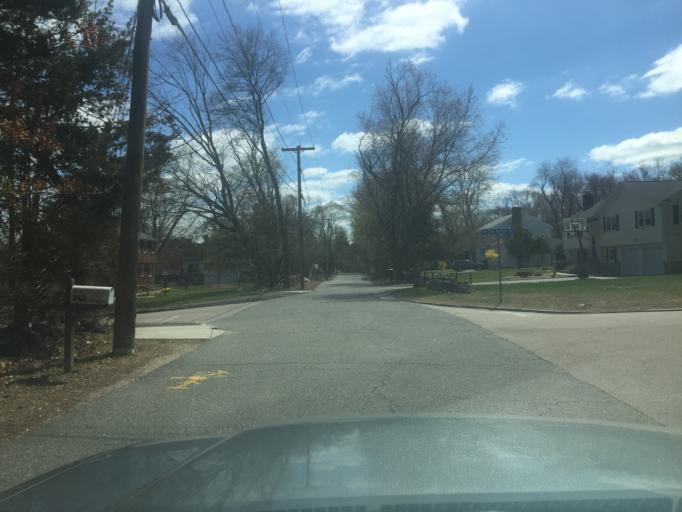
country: US
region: Massachusetts
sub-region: Norfolk County
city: Medway
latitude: 42.1664
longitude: -71.4040
